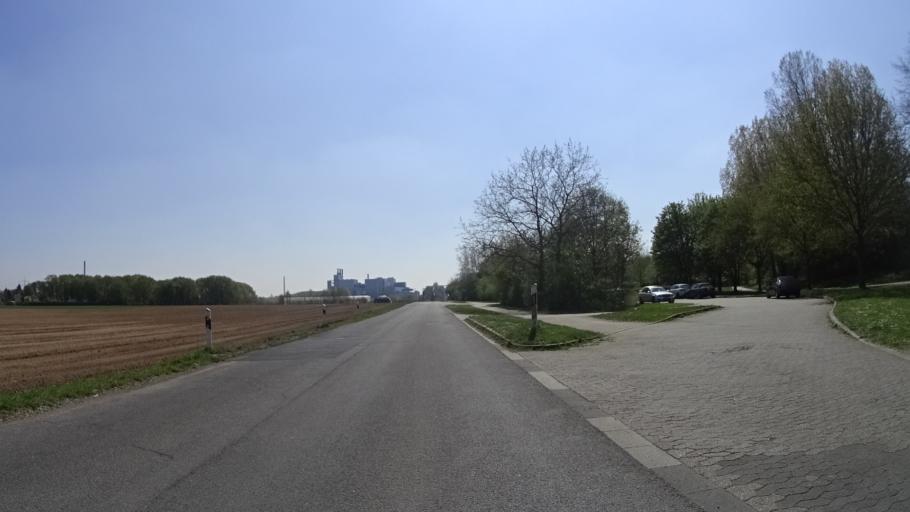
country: DE
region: North Rhine-Westphalia
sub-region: Regierungsbezirk Dusseldorf
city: Moers
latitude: 51.3886
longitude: 6.6303
